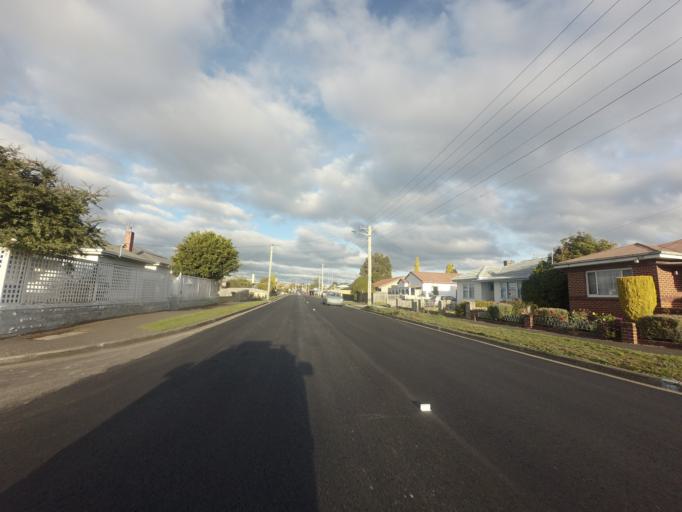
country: AU
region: Tasmania
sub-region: Glenorchy
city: Glenorchy
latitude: -42.8278
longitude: 147.2768
